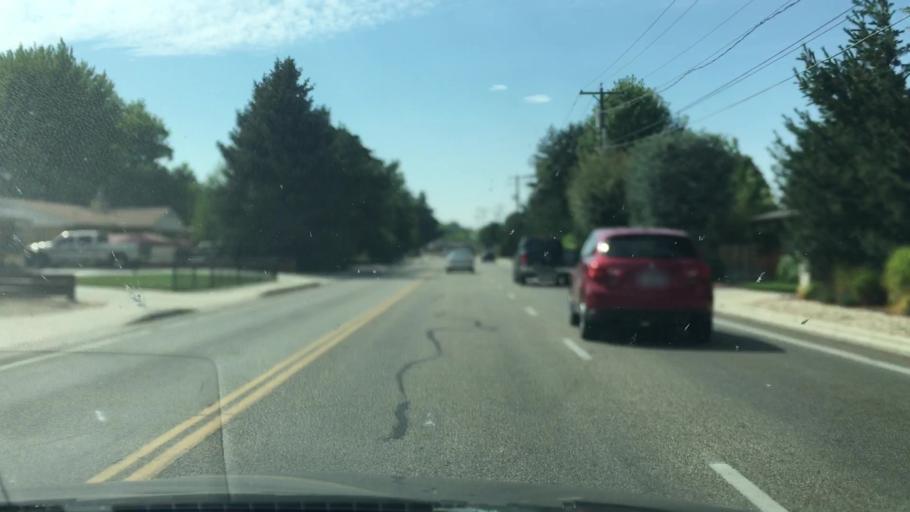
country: US
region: Idaho
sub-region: Ada County
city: Garden City
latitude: 43.6429
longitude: -116.2749
